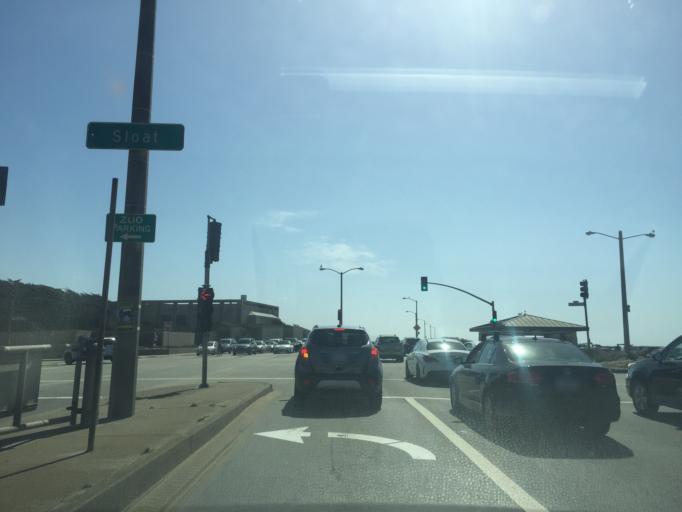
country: US
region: California
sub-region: San Mateo County
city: Daly City
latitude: 37.7359
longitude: -122.5067
